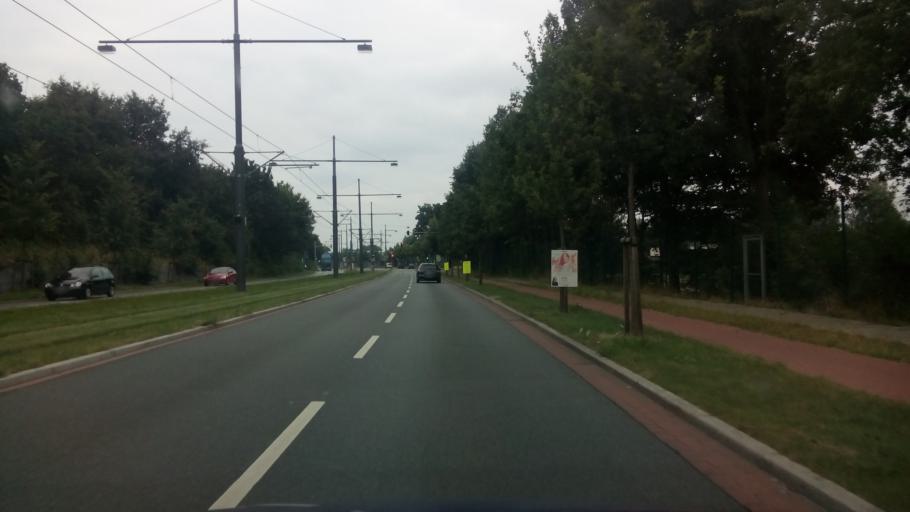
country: DE
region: Lower Saxony
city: Lilienthal
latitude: 53.1289
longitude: 8.8989
